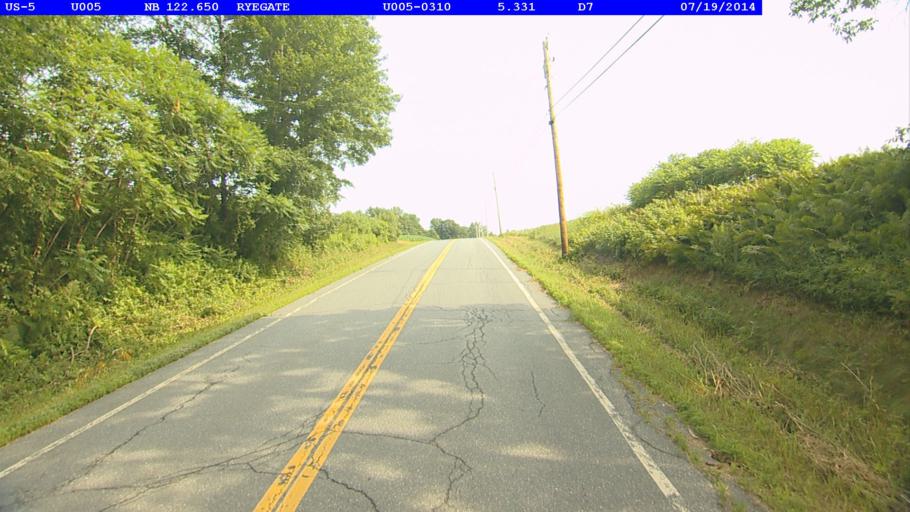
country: US
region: New Hampshire
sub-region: Grafton County
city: Woodsville
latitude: 44.2283
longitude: -72.0576
